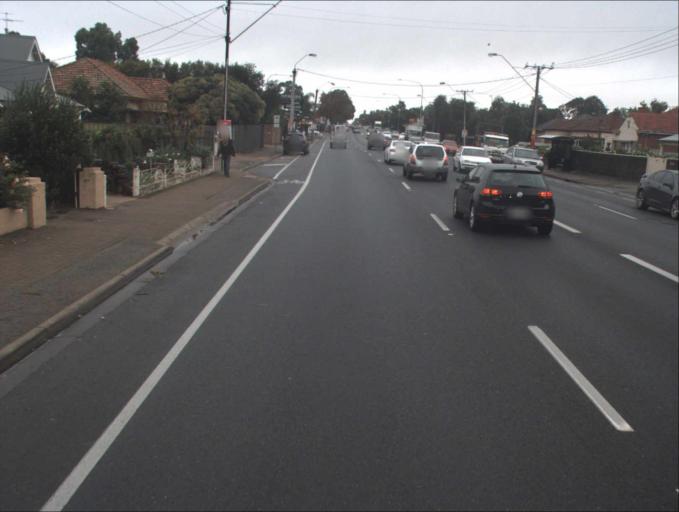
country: AU
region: South Australia
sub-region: Port Adelaide Enfield
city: Klemzig
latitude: -34.8794
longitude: 138.6197
